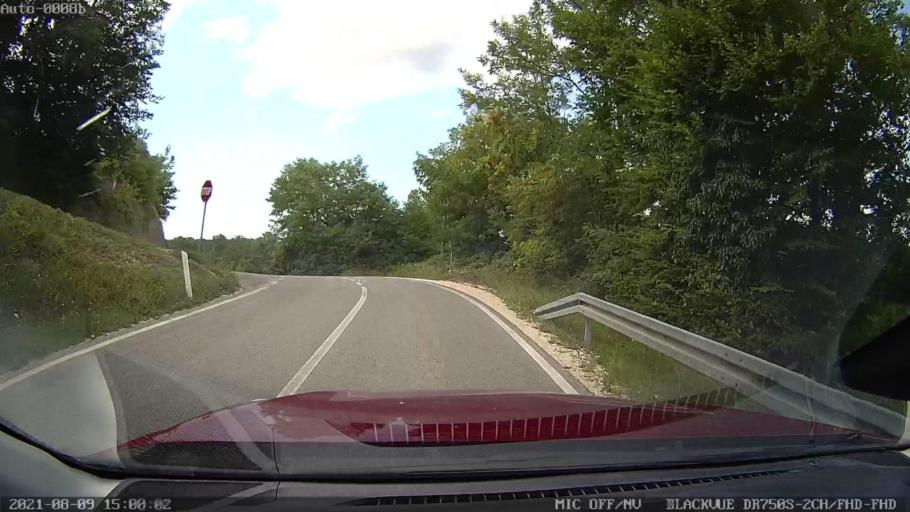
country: HR
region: Istarska
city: Pazin
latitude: 45.2704
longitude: 14.0255
